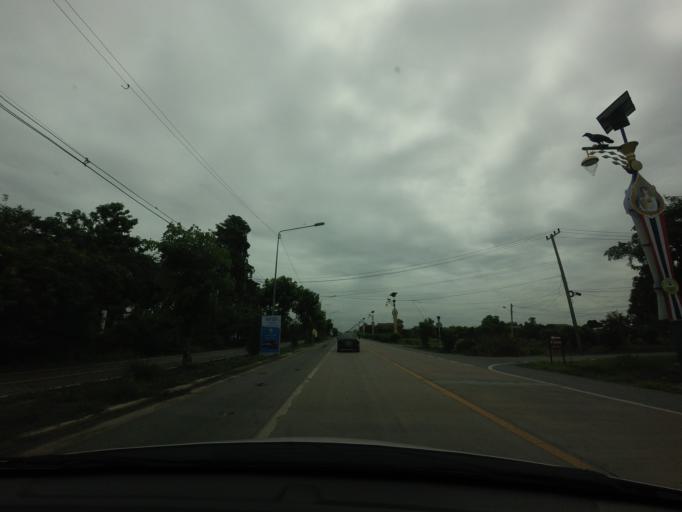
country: TH
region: Pathum Thani
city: Lam Luk Ka
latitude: 13.9302
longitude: 100.7364
